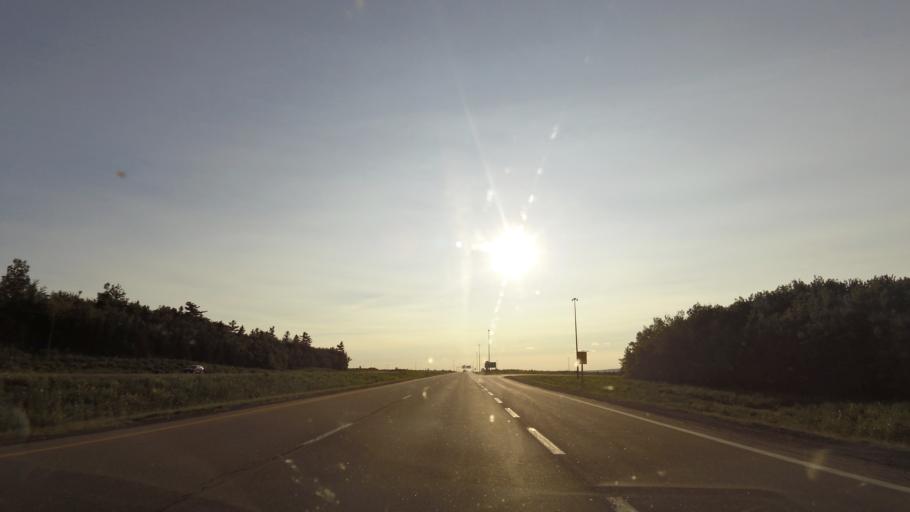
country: CA
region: New Brunswick
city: Dieppe
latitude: 46.1296
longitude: -64.6702
